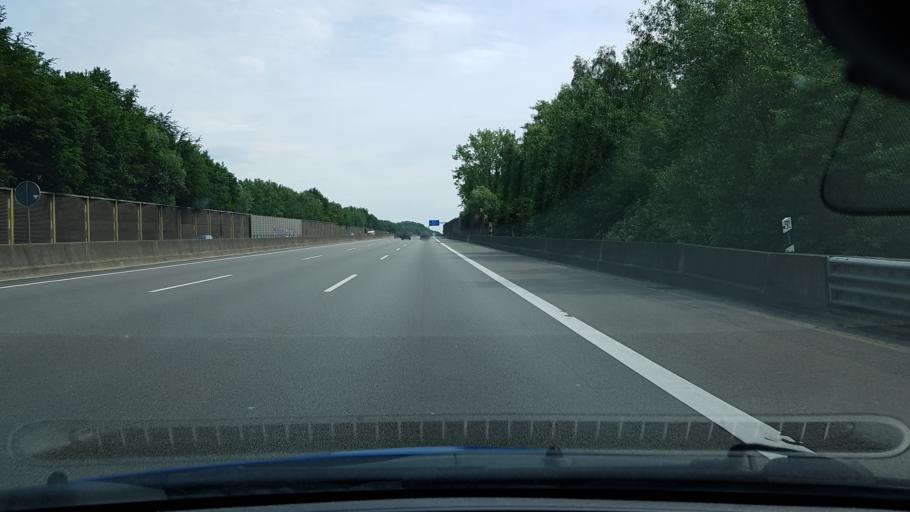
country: DE
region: Lower Saxony
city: Wallenhorst
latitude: 52.3288
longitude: 7.9808
